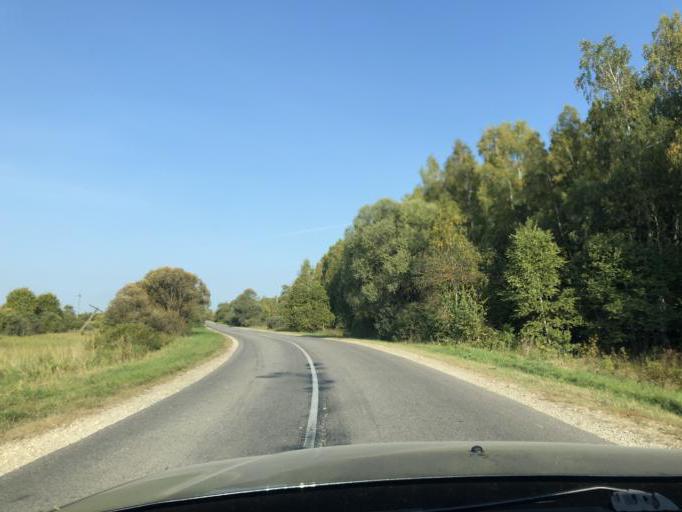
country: RU
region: Tula
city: Leninskiy
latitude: 54.3364
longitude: 37.3806
